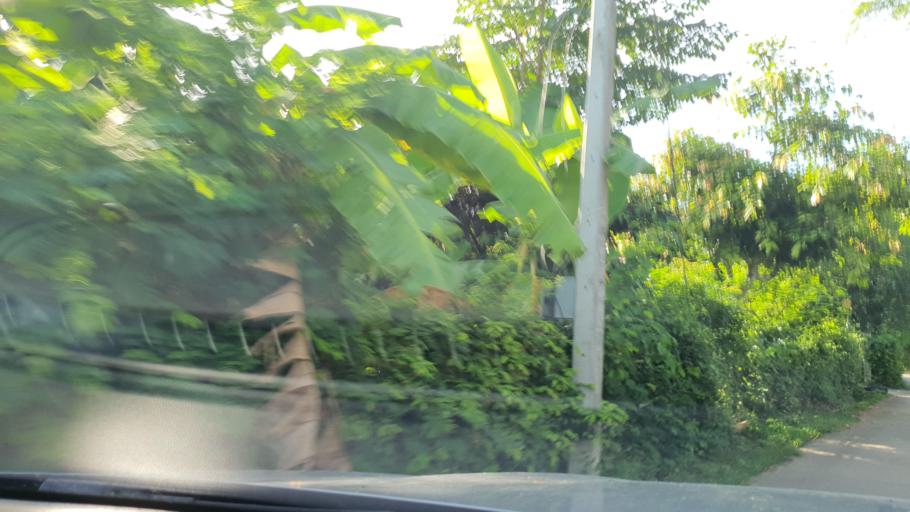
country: TH
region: Chiang Mai
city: San Kamphaeng
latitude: 18.7435
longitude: 99.1102
